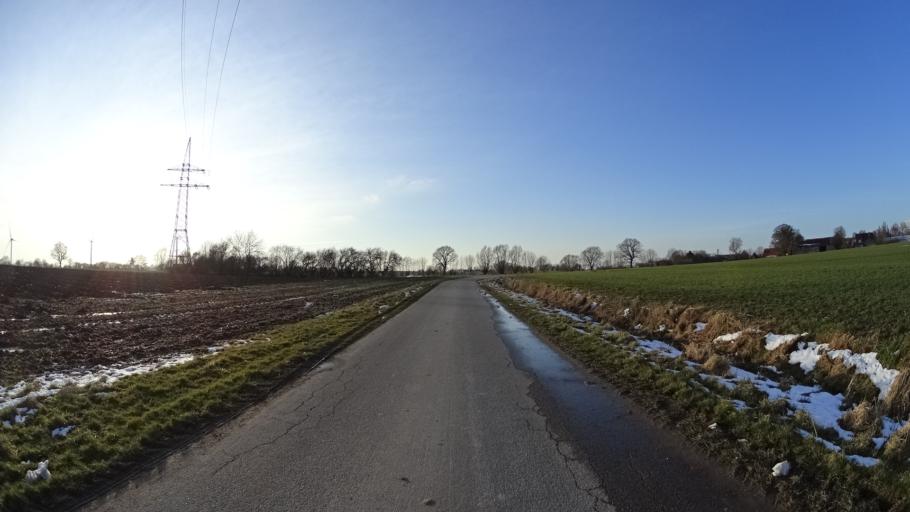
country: DE
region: Schleswig-Holstein
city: Bendfeld
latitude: 54.3593
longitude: 10.4190
